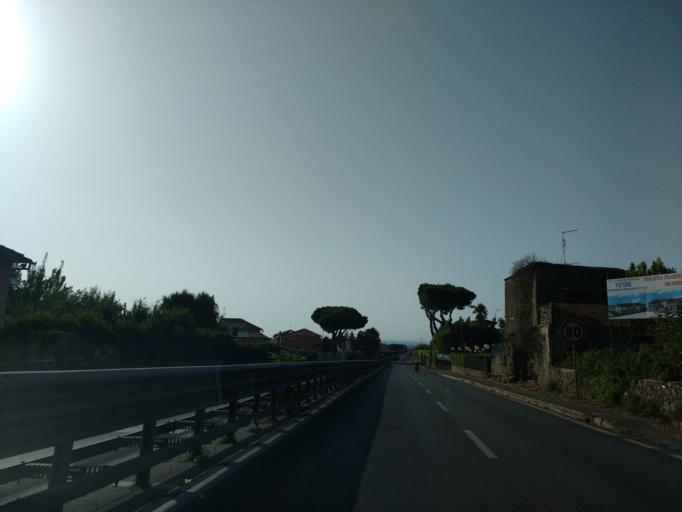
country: IT
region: Latium
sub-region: Citta metropolitana di Roma Capitale
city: Marino
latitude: 41.7616
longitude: 12.6221
